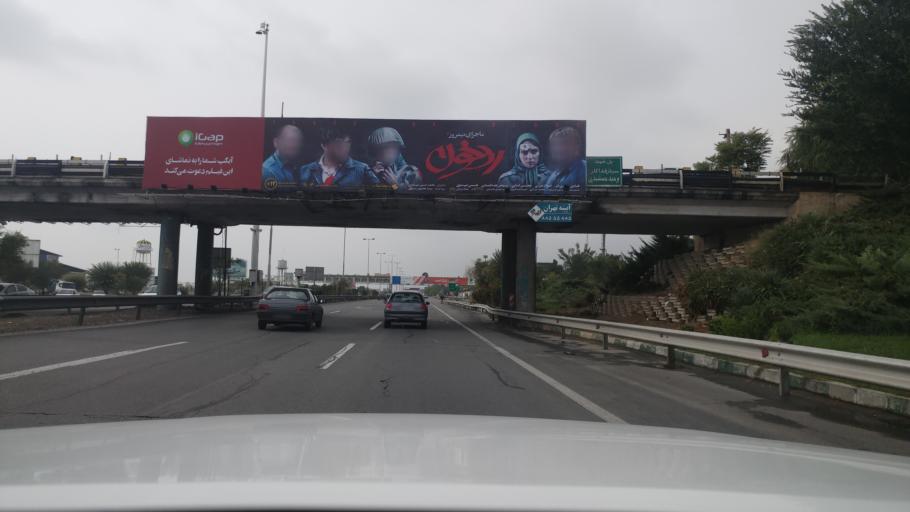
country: IR
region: Tehran
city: Shahr-e Qods
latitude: 35.7160
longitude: 51.2415
